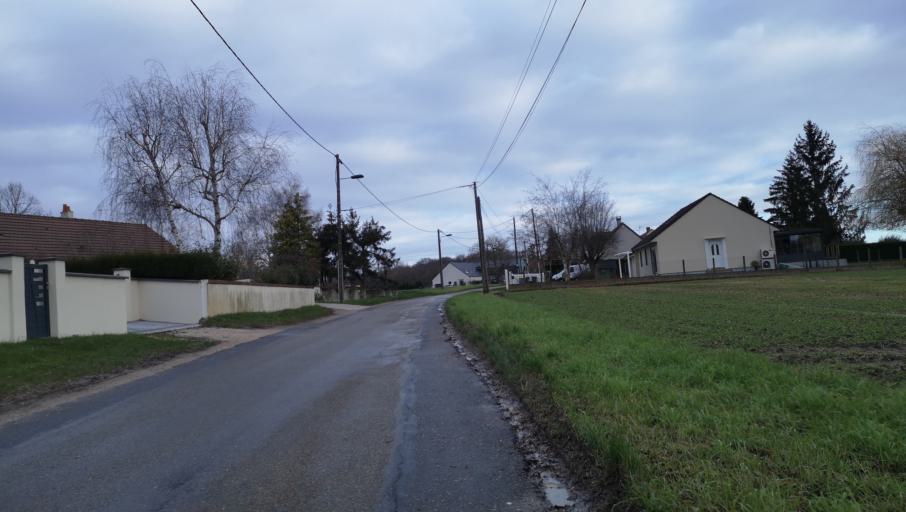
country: FR
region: Centre
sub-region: Departement du Loiret
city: Boigny-sur-Bionne
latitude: 47.9121
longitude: 2.0032
